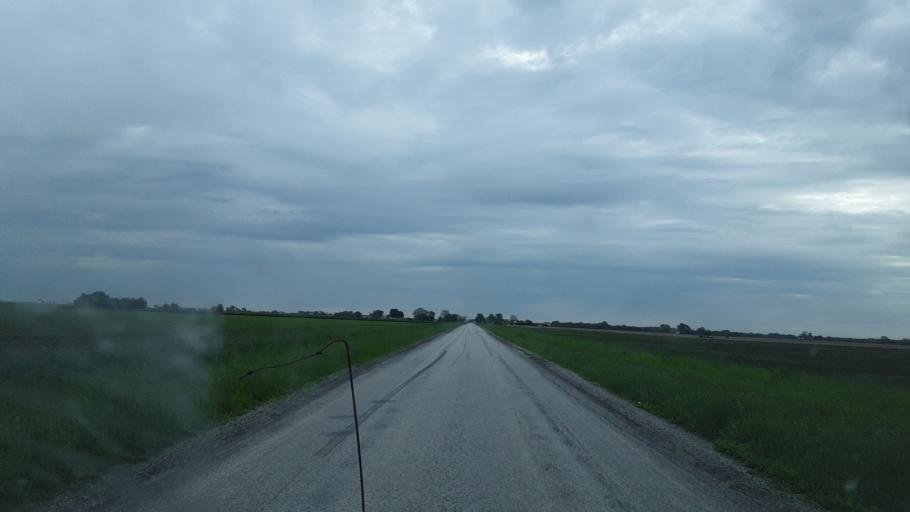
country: US
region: Illinois
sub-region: McDonough County
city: Macomb
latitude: 40.3819
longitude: -90.6716
